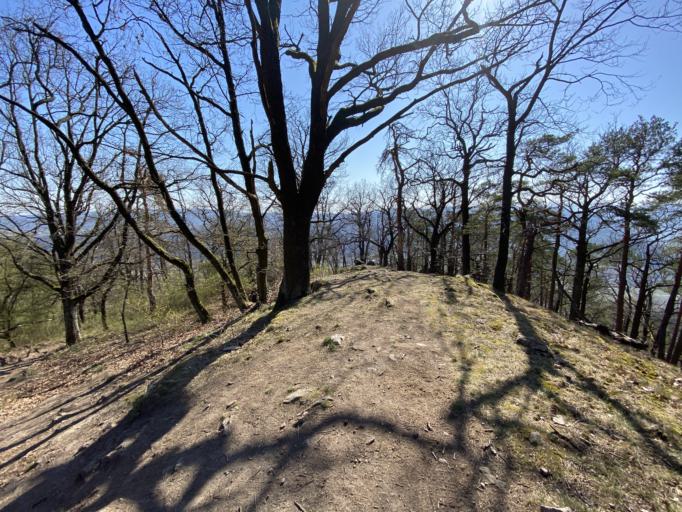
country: AT
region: Lower Austria
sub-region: Politischer Bezirk Krems
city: Durnstein
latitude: 48.4034
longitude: 15.5292
